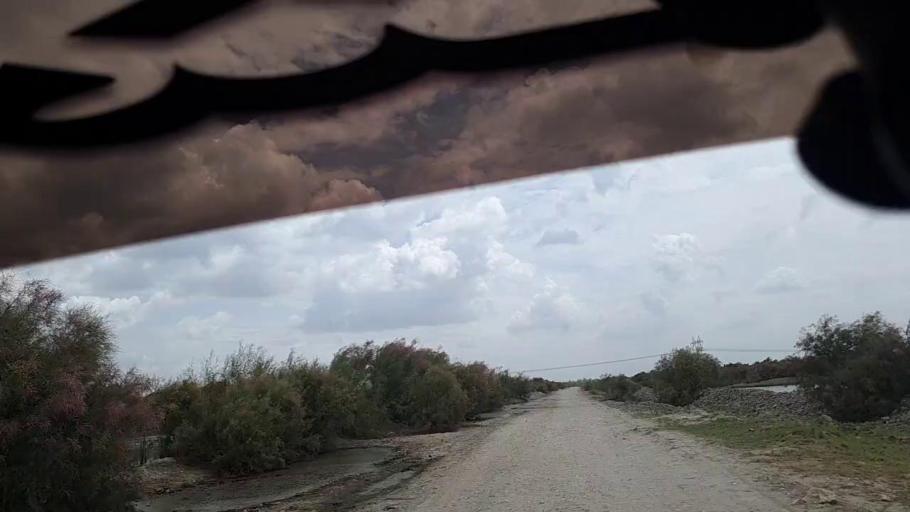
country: PK
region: Sindh
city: Ghauspur
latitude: 28.0693
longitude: 68.9376
